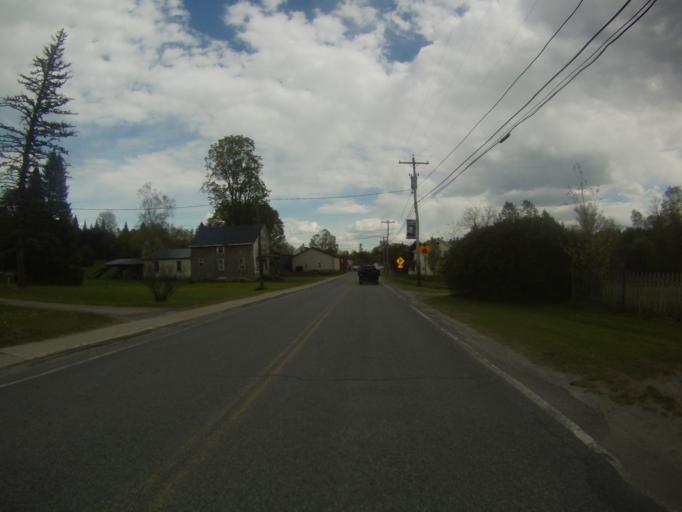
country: US
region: New York
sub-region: Essex County
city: Mineville
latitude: 44.0632
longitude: -73.5122
